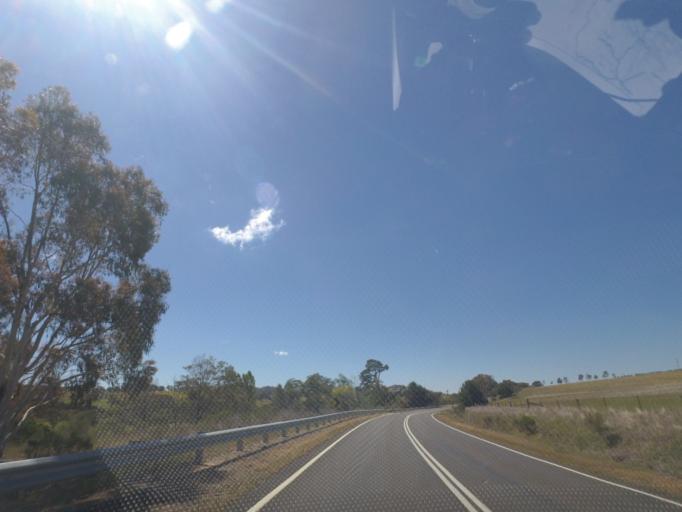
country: AU
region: Victoria
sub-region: Hume
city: Sunbury
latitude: -37.0861
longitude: 144.7592
